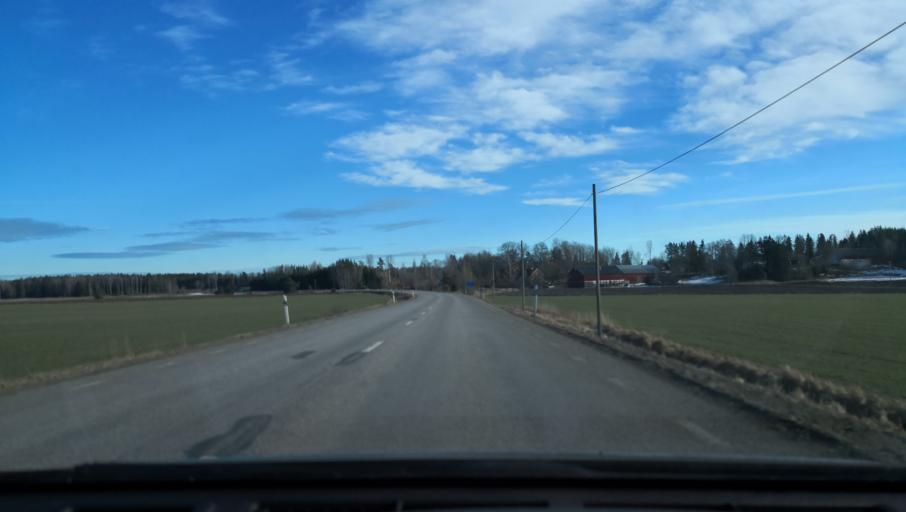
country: SE
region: Uppsala
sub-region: Osthammars Kommun
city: Osterbybruk
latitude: 60.1643
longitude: 17.9791
